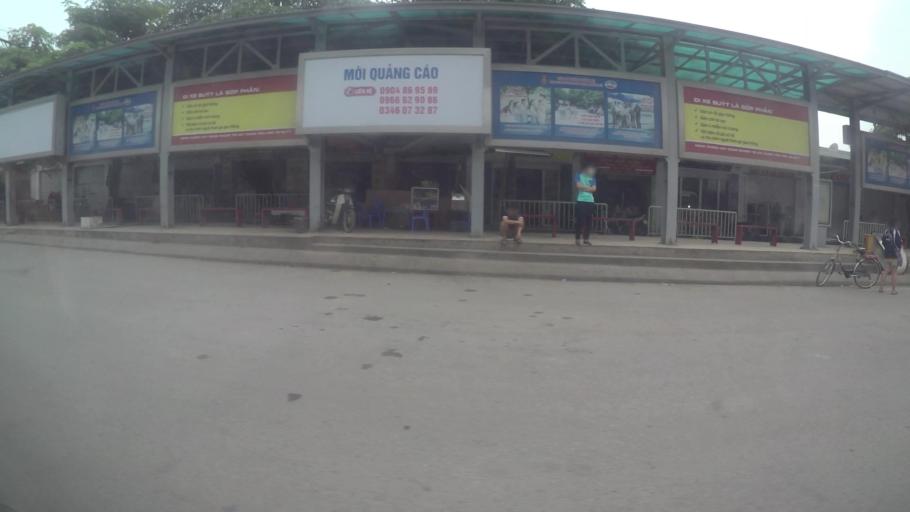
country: VN
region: Ha Noi
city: Cau Dien
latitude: 21.0510
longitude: 105.7374
